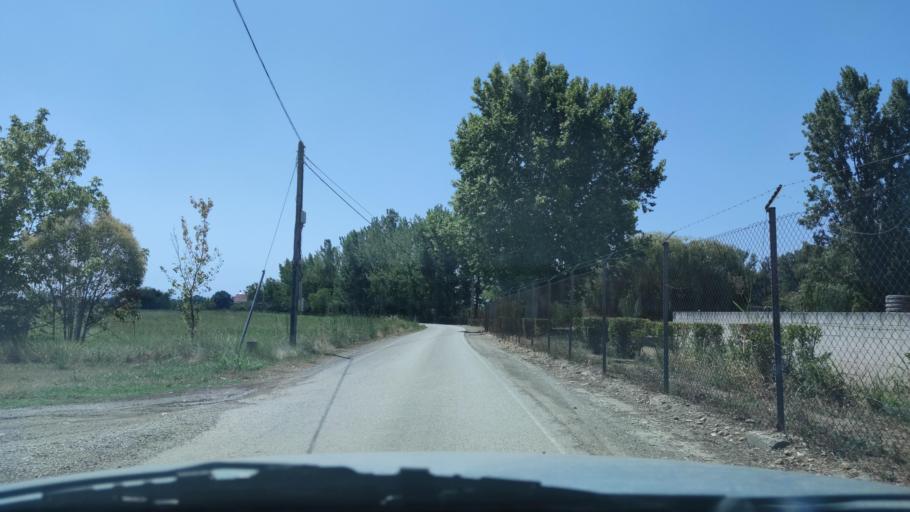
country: ES
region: Catalonia
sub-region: Provincia de Lleida
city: Alpicat
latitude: 41.6464
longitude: 0.5731
